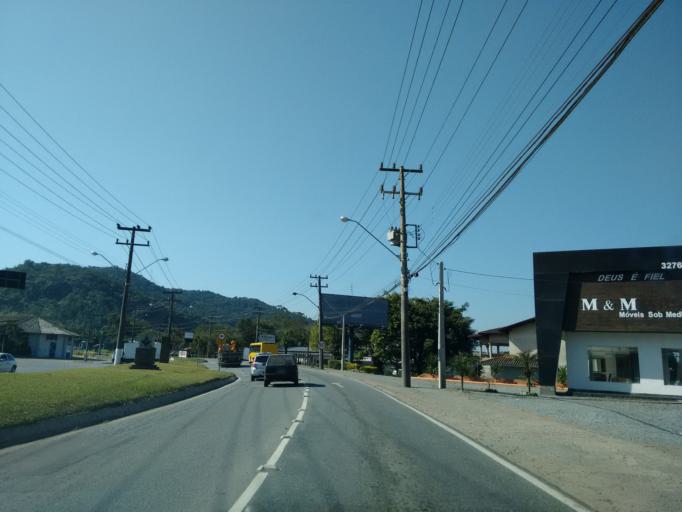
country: BR
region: Santa Catarina
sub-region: Guaramirim
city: Guaramirim
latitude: -26.4785
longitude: -49.0334
